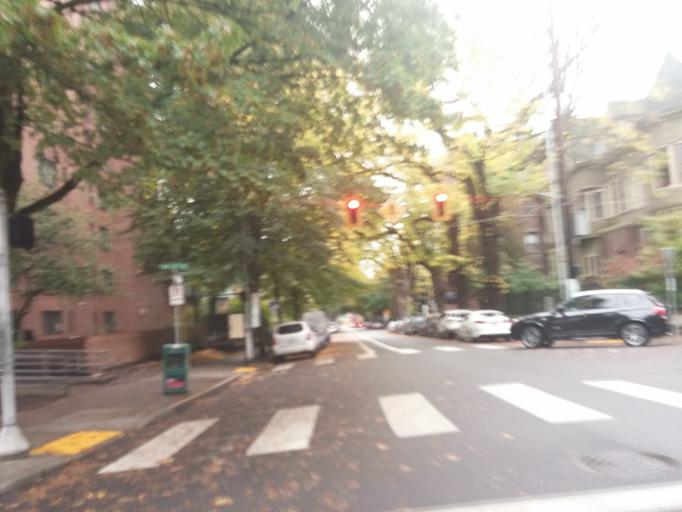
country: US
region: Oregon
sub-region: Multnomah County
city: Portland
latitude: 45.5249
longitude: -122.6937
